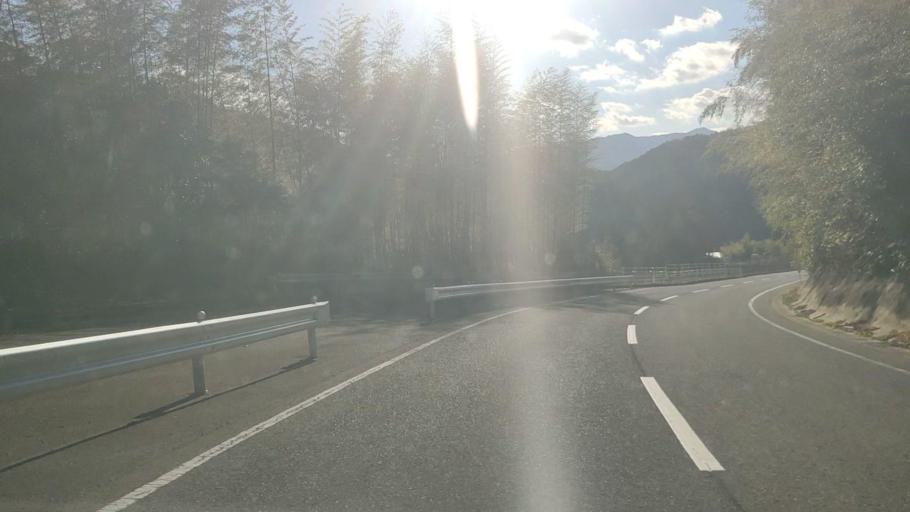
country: JP
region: Saga Prefecture
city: Kanzakimachi-kanzaki
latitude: 33.3897
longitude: 130.2658
